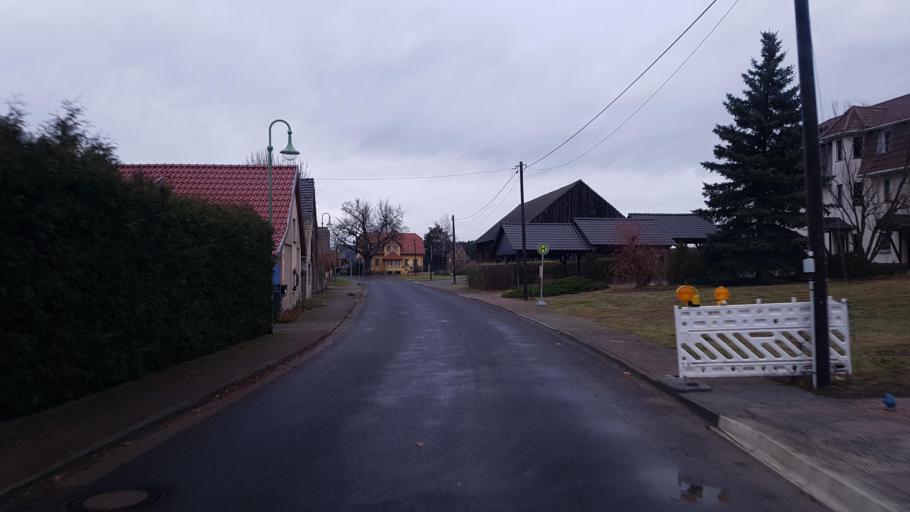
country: DE
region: Brandenburg
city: Tauche
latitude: 52.0588
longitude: 14.1106
